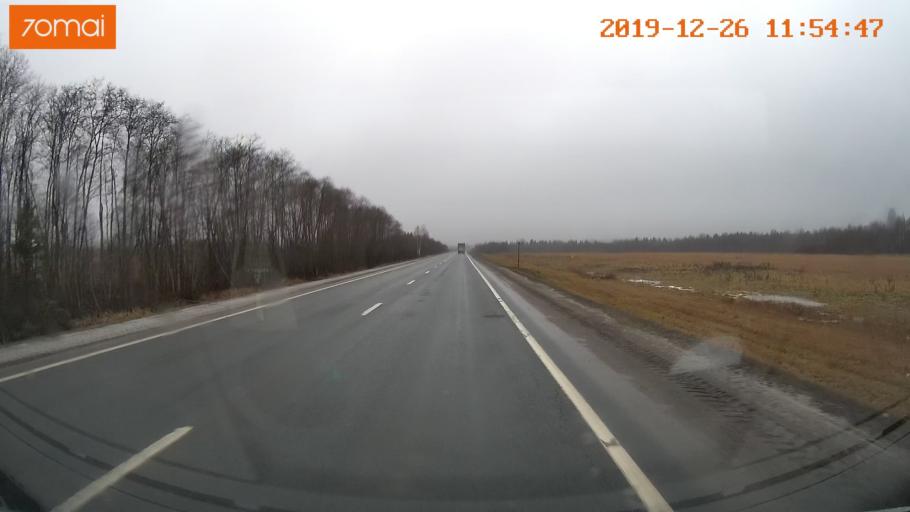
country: RU
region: Vologda
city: Sheksna
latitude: 59.2777
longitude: 38.2978
